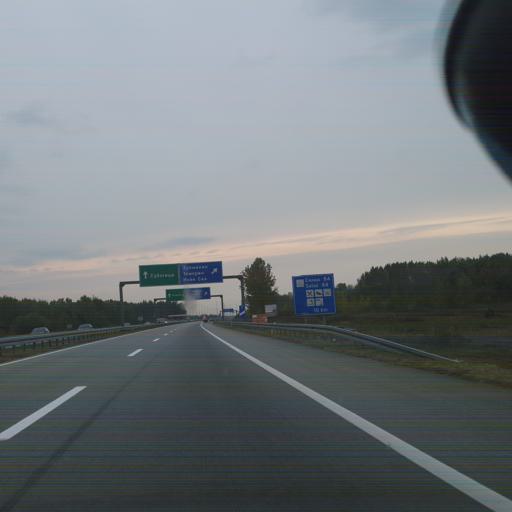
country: RS
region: Autonomna Pokrajina Vojvodina
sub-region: Juznobacki Okrug
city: Petrovaradin
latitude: 45.2844
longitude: 19.8979
